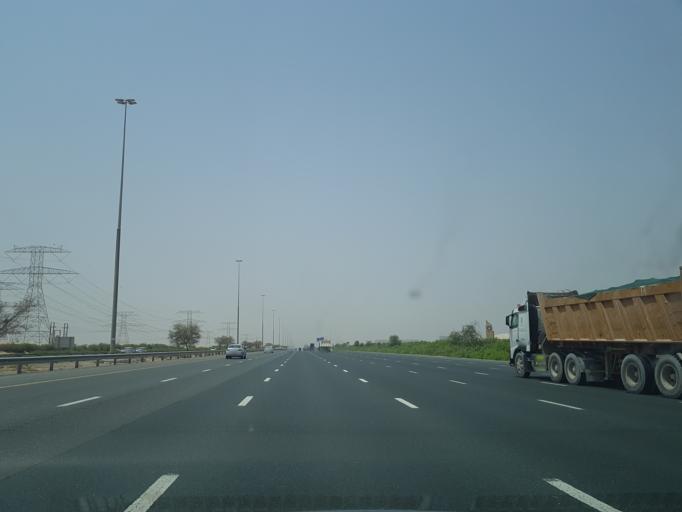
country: AE
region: Ash Shariqah
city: Sharjah
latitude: 25.1072
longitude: 55.4209
